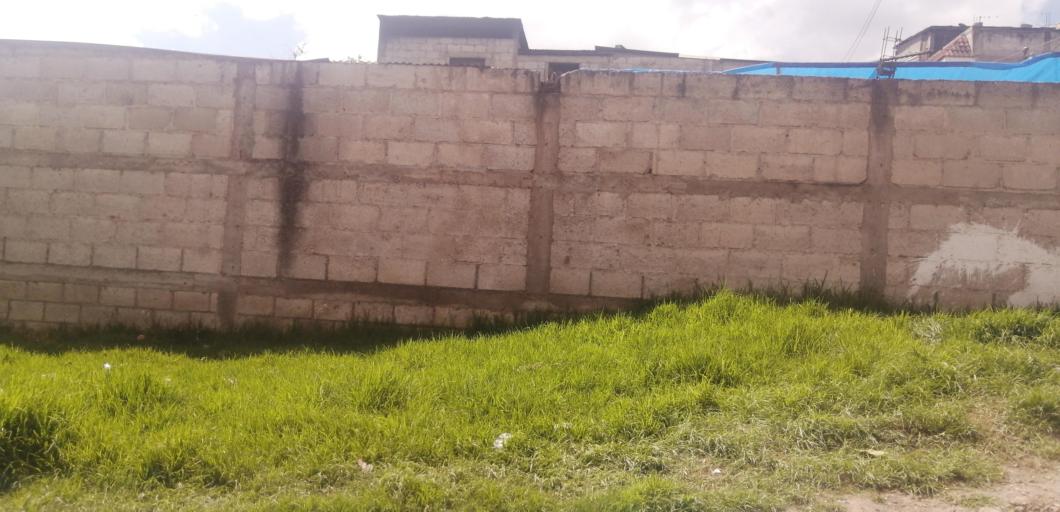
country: GT
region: Quetzaltenango
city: Quetzaltenango
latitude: 14.8351
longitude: -91.5310
